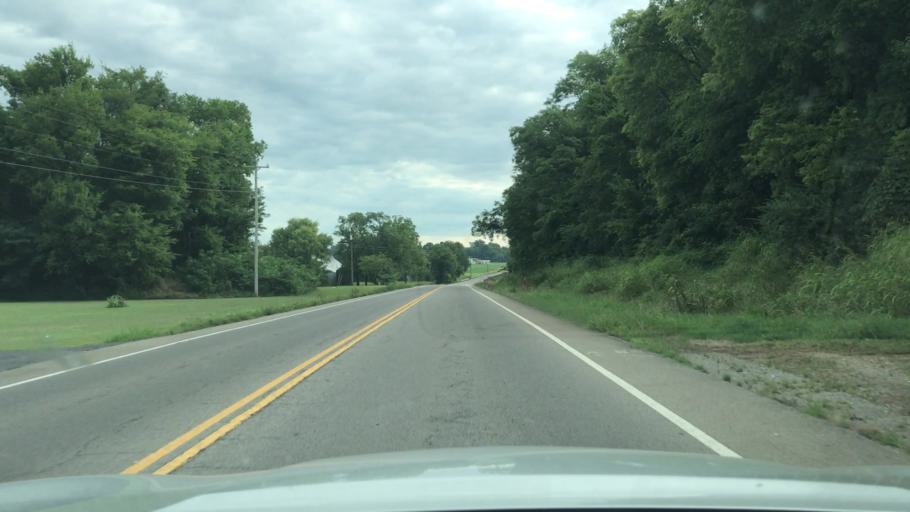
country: US
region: Kentucky
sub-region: Todd County
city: Guthrie
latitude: 36.6330
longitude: -87.2144
